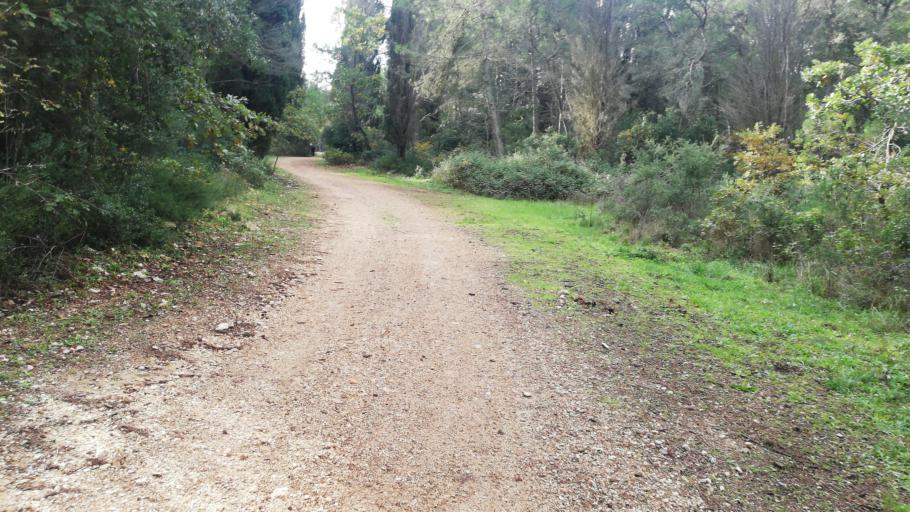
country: IT
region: Apulia
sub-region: Provincia di Bari
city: Cassano delle Murge
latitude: 40.8716
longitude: 16.7137
